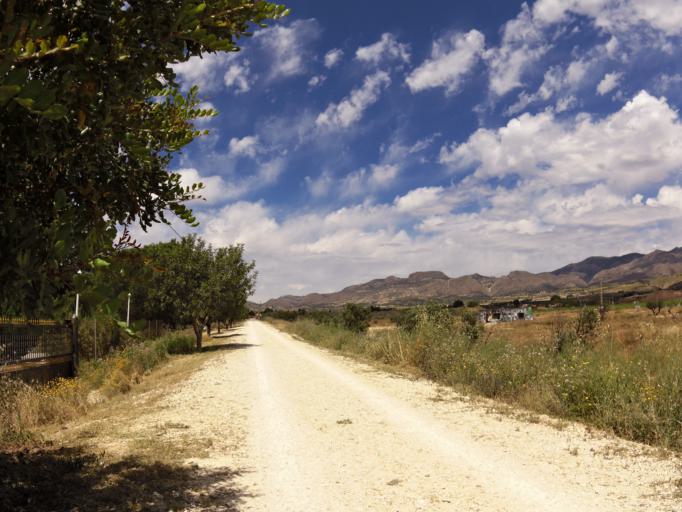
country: ES
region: Valencia
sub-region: Provincia de Alicante
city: Agost
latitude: 38.4372
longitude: -0.6465
